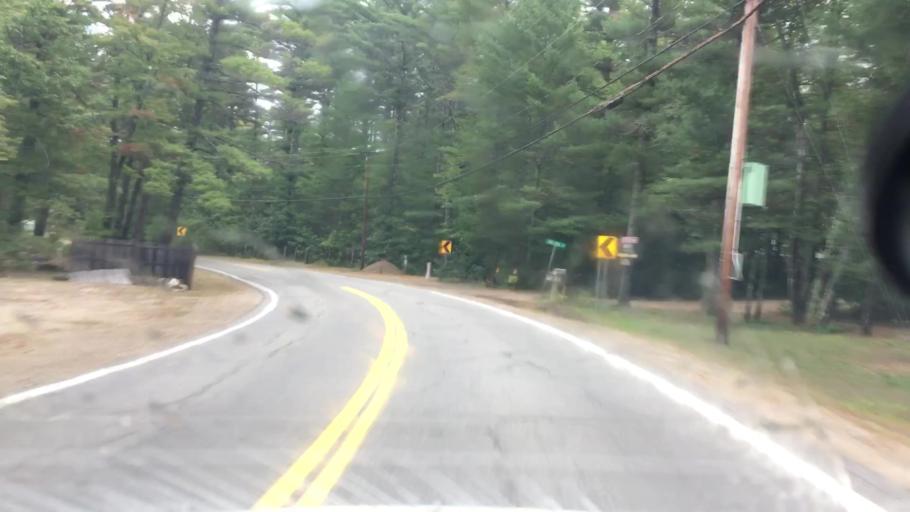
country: US
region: New Hampshire
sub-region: Carroll County
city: Wakefield
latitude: 43.6277
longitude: -70.9847
